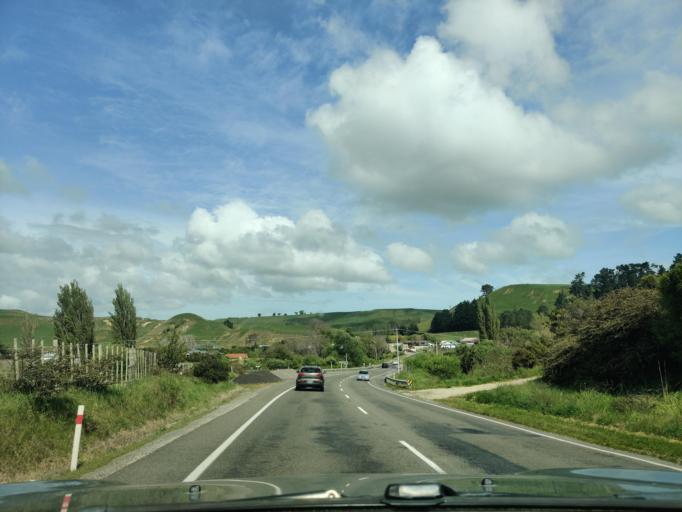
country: NZ
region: Manawatu-Wanganui
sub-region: Wanganui District
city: Wanganui
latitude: -39.8450
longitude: 174.9255
